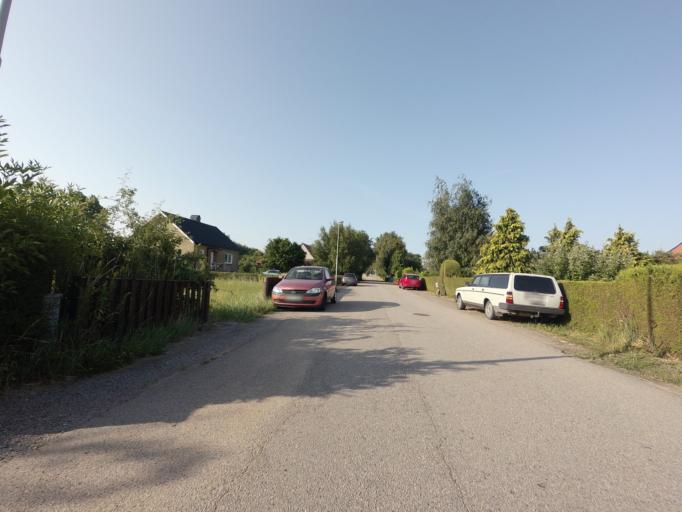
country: SE
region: Skane
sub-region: Landskrona
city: Landskrona
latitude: 55.8731
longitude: 12.8727
